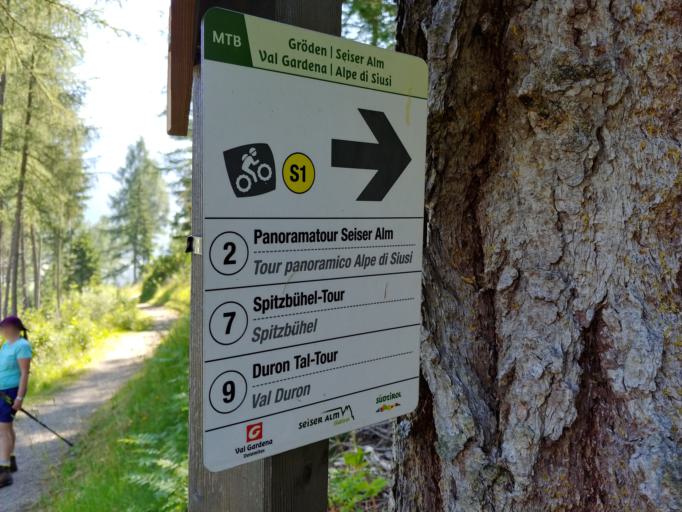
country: IT
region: Trentino-Alto Adige
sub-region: Bolzano
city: Santa Cristina Valgardena
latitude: 46.5532
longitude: 11.7194
